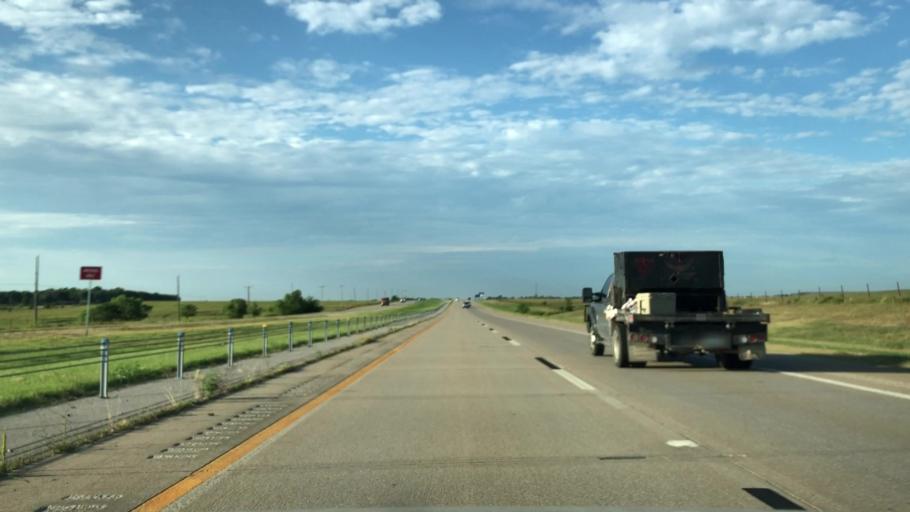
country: US
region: Oklahoma
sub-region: Osage County
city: Skiatook
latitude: 36.3870
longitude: -95.9205
